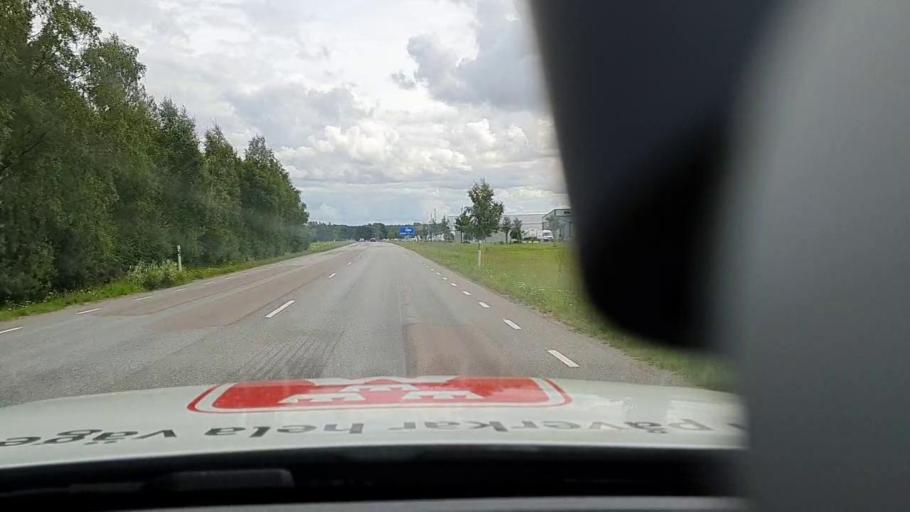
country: SE
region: Vaestra Goetaland
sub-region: Lidkopings Kommun
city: Lidkoping
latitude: 58.5071
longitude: 13.1214
